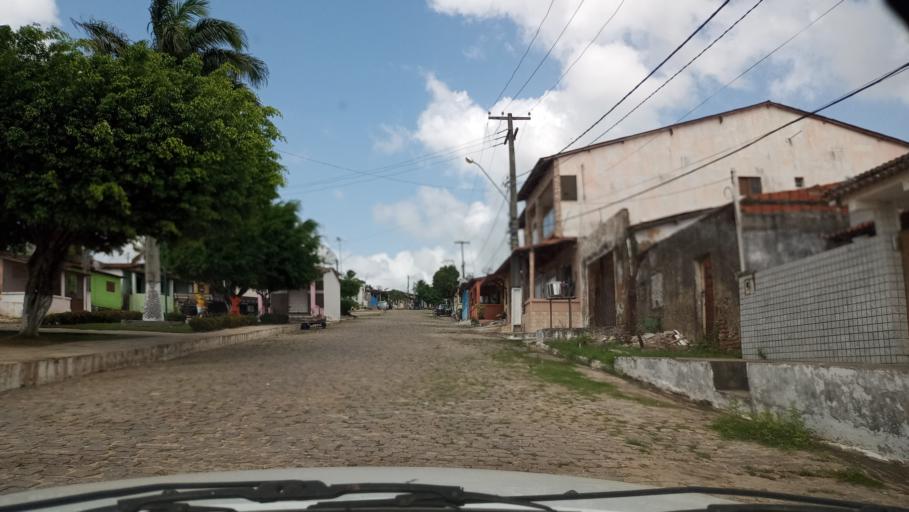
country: BR
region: Rio Grande do Norte
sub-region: Ares
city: Ares
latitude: -6.2357
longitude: -35.1341
